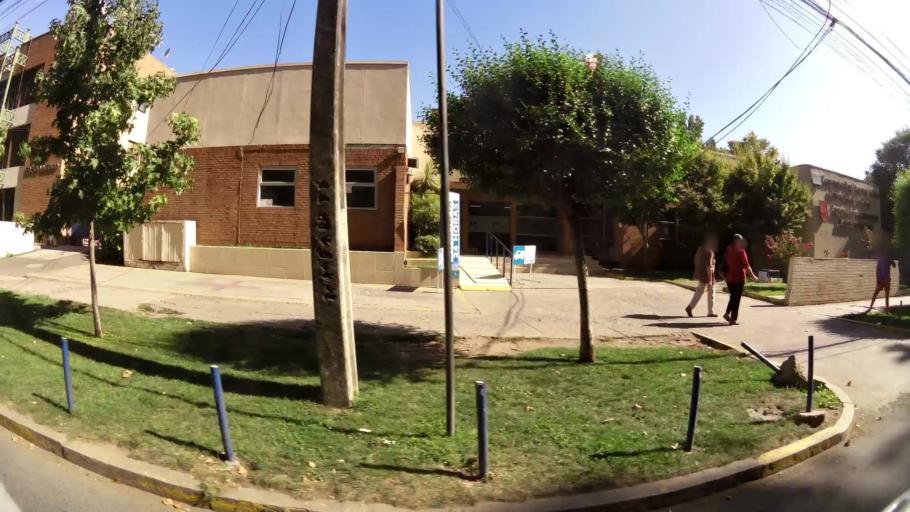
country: CL
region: Maule
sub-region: Provincia de Talca
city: Talca
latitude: -35.4232
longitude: -71.6532
